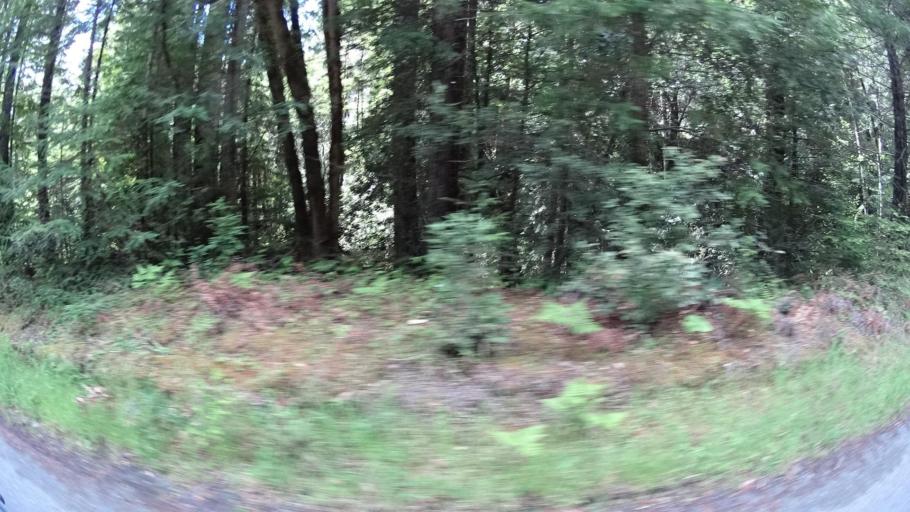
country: US
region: California
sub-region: Humboldt County
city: Blue Lake
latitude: 40.8464
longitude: -123.8961
